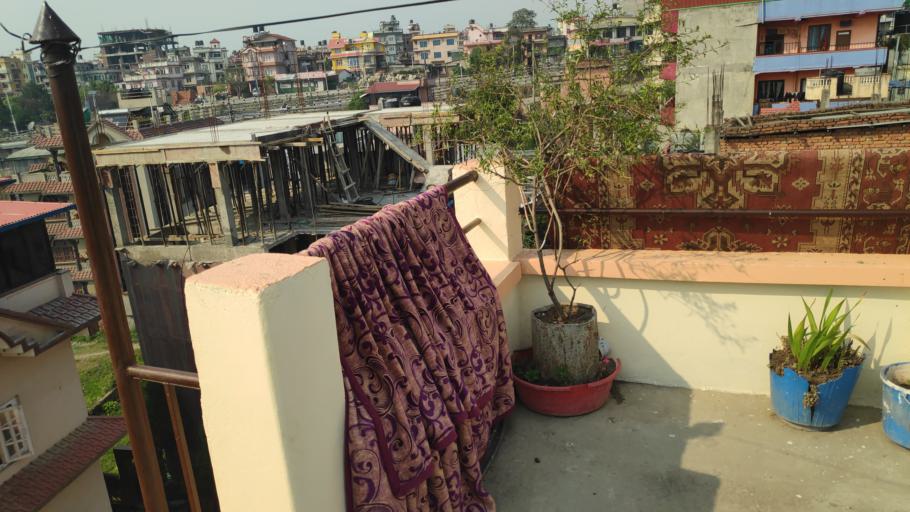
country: NP
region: Central Region
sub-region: Bagmati Zone
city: Patan
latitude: 27.6732
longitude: 85.3680
